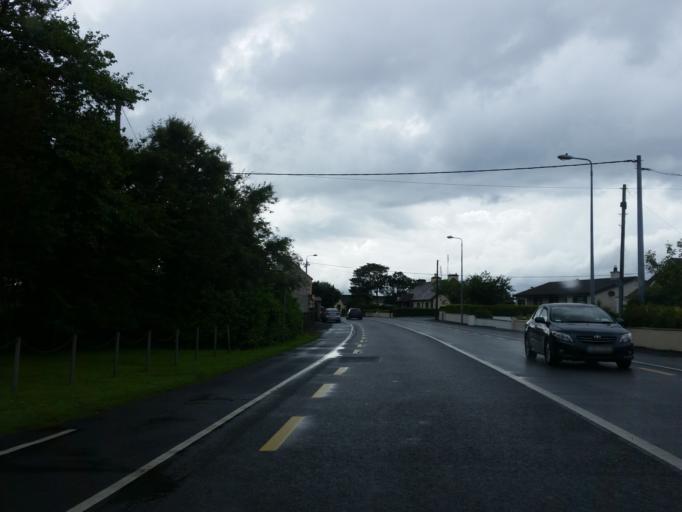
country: IE
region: Connaught
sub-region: Sligo
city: Strandhill
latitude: 54.2704
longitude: -8.5886
